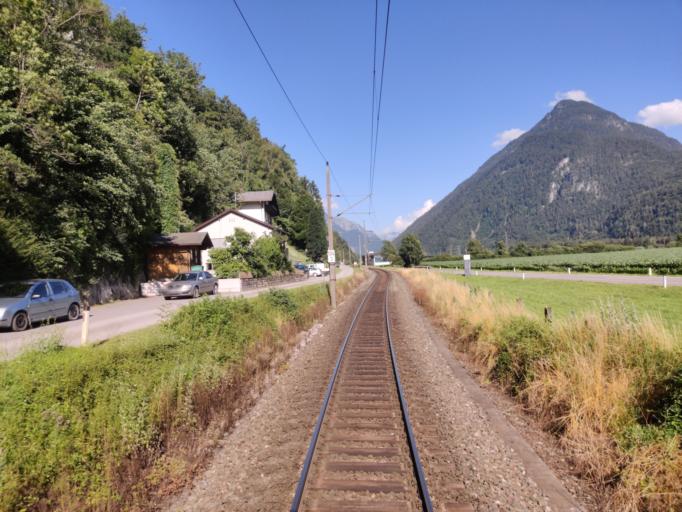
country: AT
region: Vorarlberg
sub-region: Politischer Bezirk Bludenz
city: Bludenz
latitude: 47.1456
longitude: 9.8338
